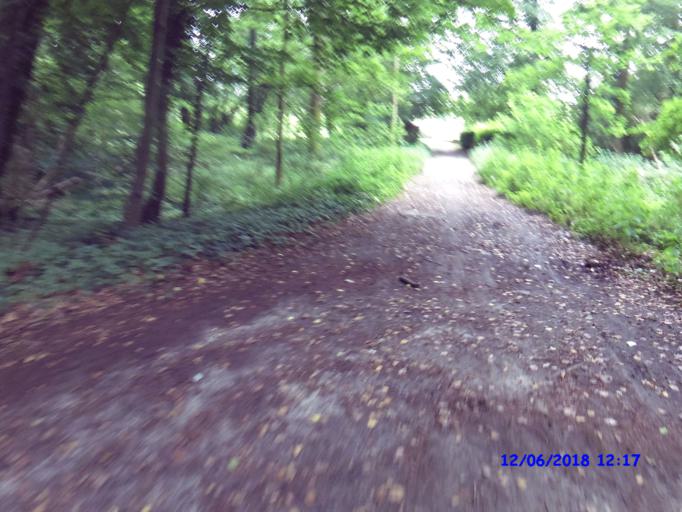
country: BE
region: Flanders
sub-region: Provincie Vlaams-Brabant
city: Oud-Heverlee
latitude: 50.8248
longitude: 4.6722
